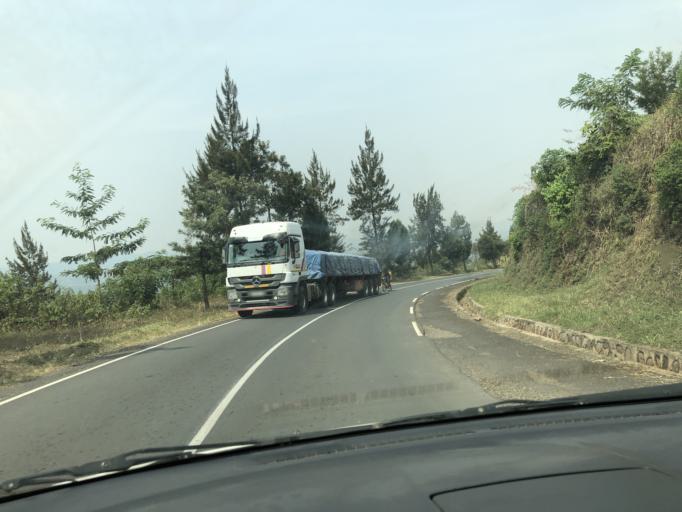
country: RW
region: Western Province
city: Cyangugu
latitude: -2.6705
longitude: 29.0035
